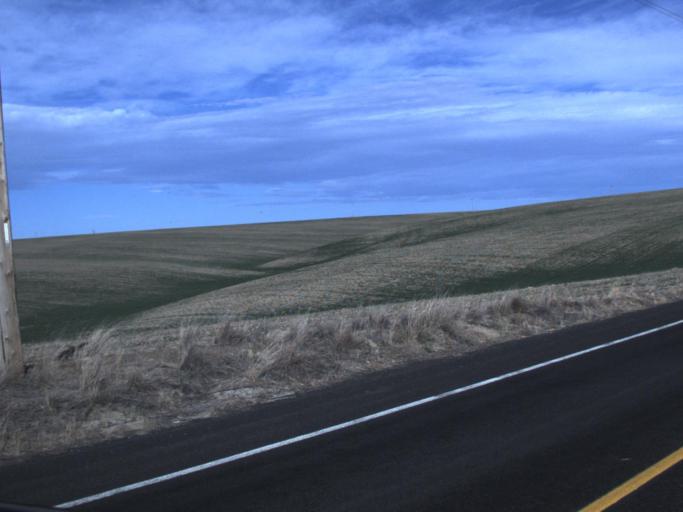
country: US
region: Washington
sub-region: Adams County
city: Ritzville
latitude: 47.1254
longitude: -118.6651
